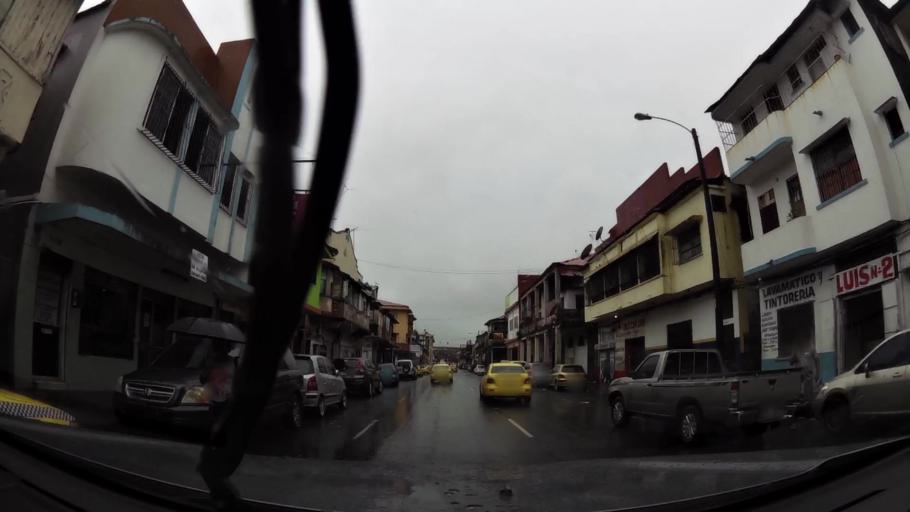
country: PA
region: Colon
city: Colon
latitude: 9.3552
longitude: -79.9021
